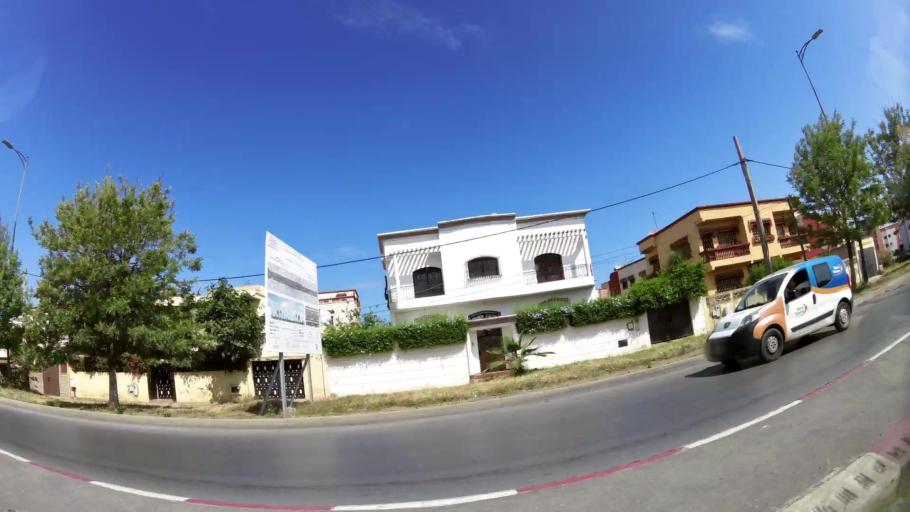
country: MA
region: Rabat-Sale-Zemmour-Zaer
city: Sale
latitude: 34.0665
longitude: -6.7943
